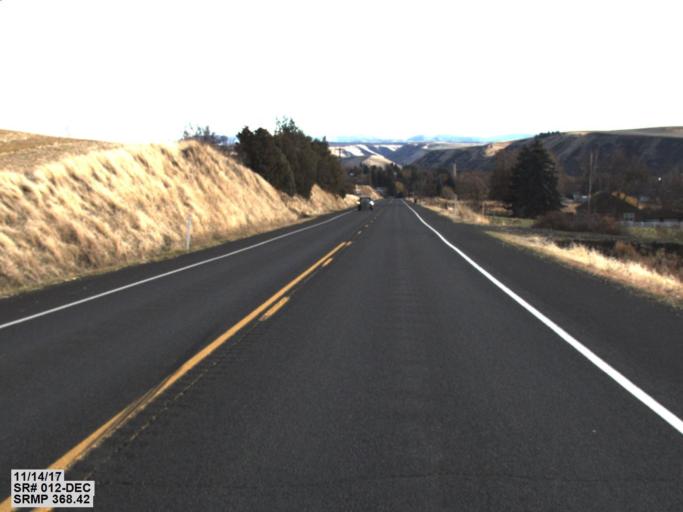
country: US
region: Washington
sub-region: Columbia County
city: Dayton
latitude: 46.3343
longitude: -117.9782
